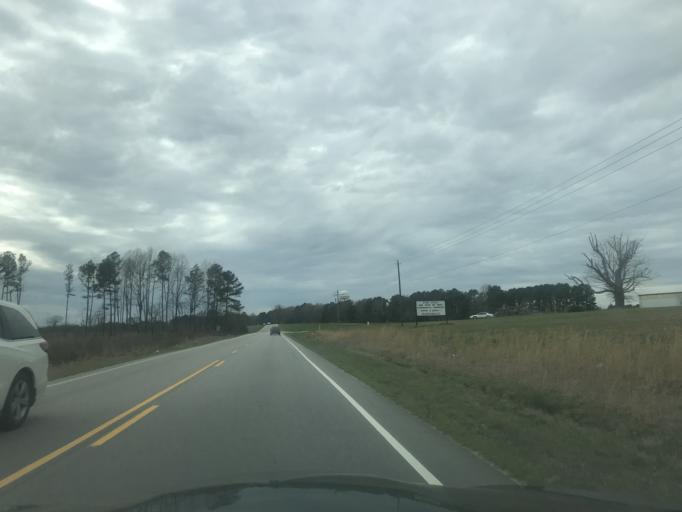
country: US
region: North Carolina
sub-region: Franklin County
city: Franklinton
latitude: 36.0926
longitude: -78.4029
